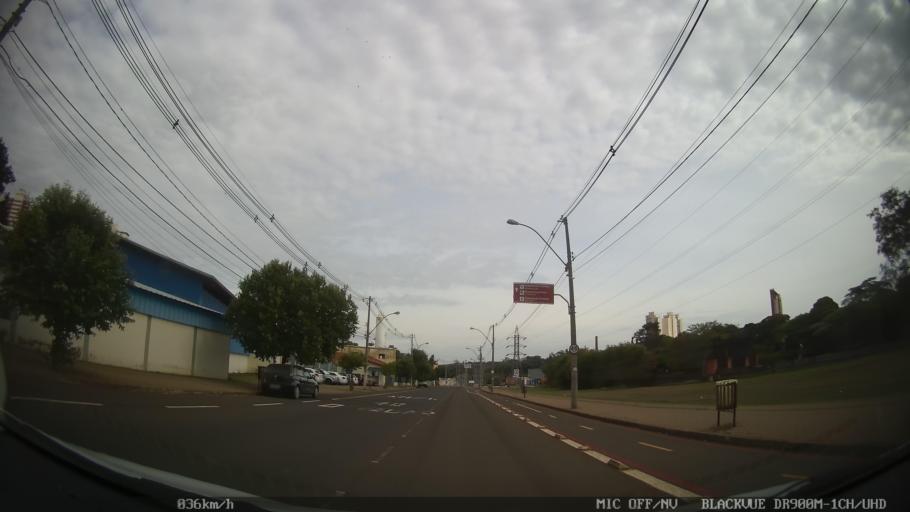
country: BR
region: Sao Paulo
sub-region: Piracicaba
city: Piracicaba
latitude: -22.7170
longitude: -47.6514
